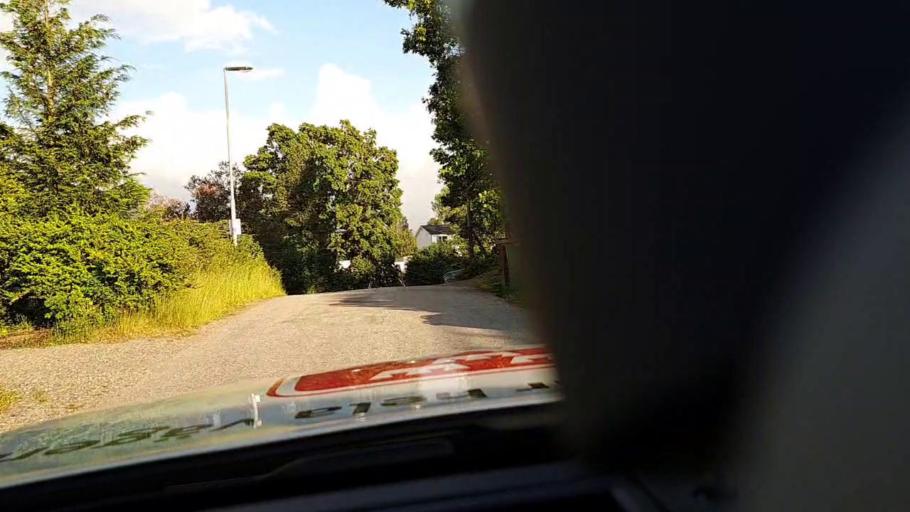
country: SE
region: Stockholm
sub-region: Huddinge Kommun
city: Huddinge
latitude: 59.2458
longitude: 17.9705
